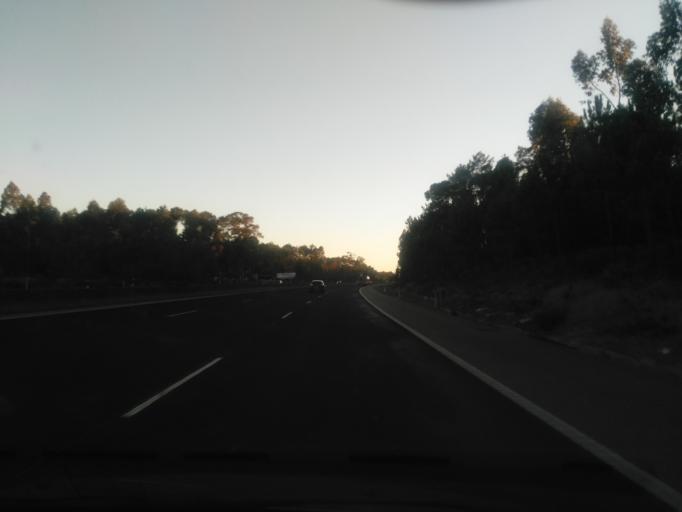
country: PT
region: Leiria
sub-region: Leiria
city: Maceira
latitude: 39.7001
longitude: -8.9231
